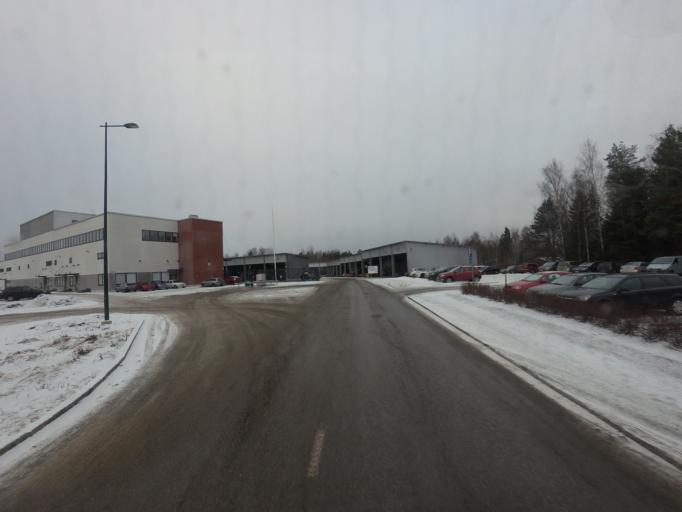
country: FI
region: Uusimaa
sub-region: Helsinki
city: Espoo
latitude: 60.2104
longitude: 24.6371
